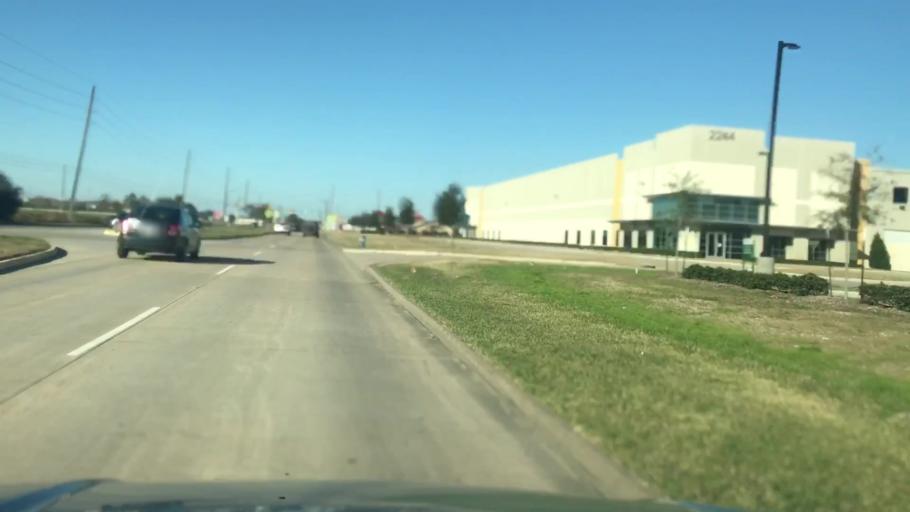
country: US
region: Texas
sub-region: Fort Bend County
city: Cinco Ranch
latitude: 29.8070
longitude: -95.7520
